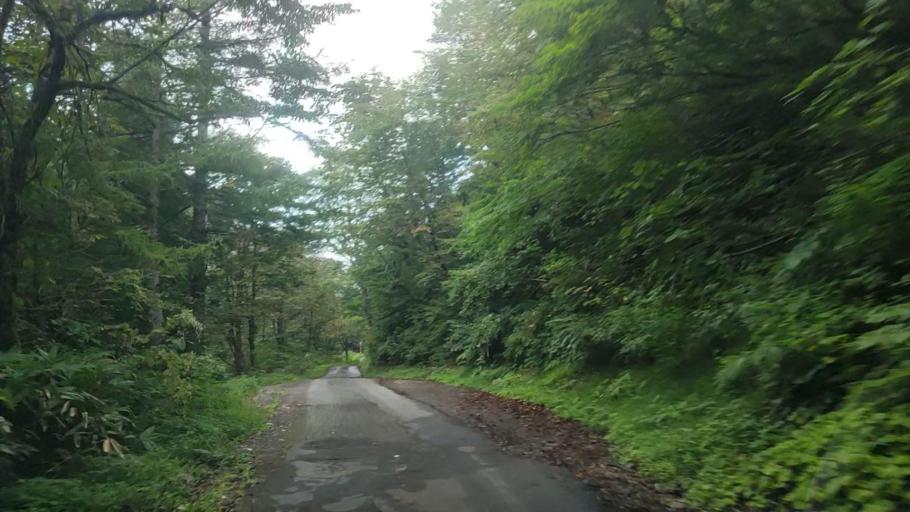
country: JP
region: Toyama
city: Yatsuomachi-higashikumisaka
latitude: 36.4037
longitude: 137.0754
